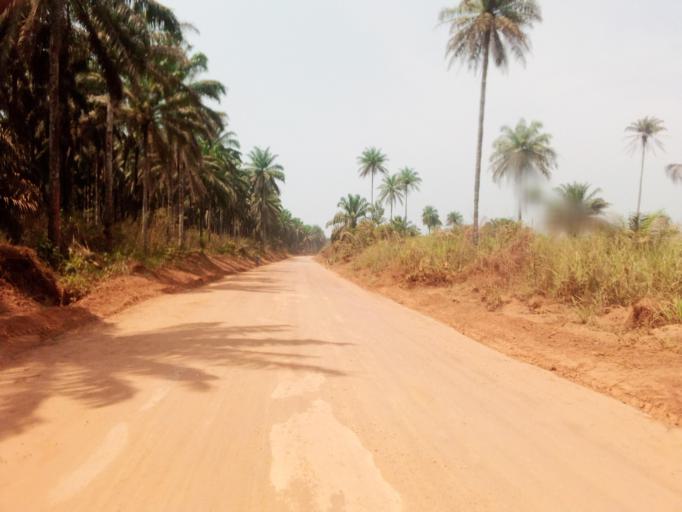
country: SL
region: Southern Province
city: Sumbuya
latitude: 7.6198
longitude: -12.1187
